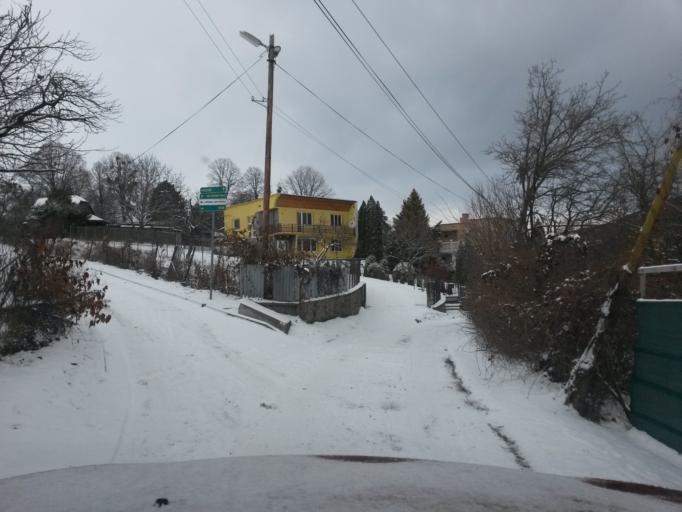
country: HU
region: Borsod-Abauj-Zemplen
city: Gonc
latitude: 48.5914
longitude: 21.3780
